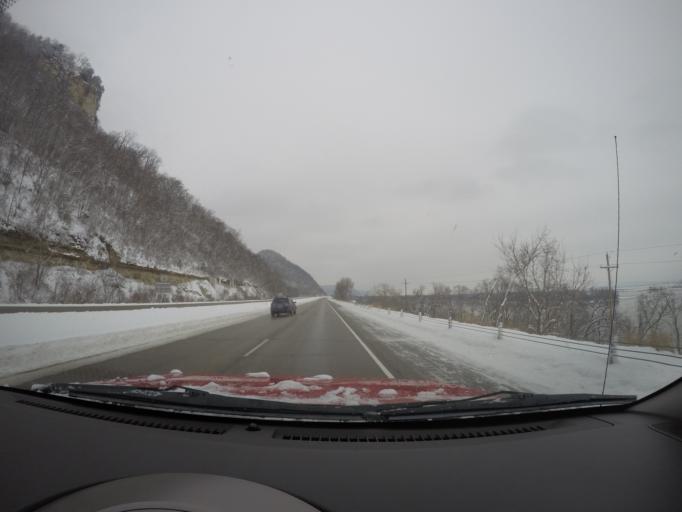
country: US
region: Minnesota
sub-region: Houston County
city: La Crescent
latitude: 43.8712
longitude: -91.3174
